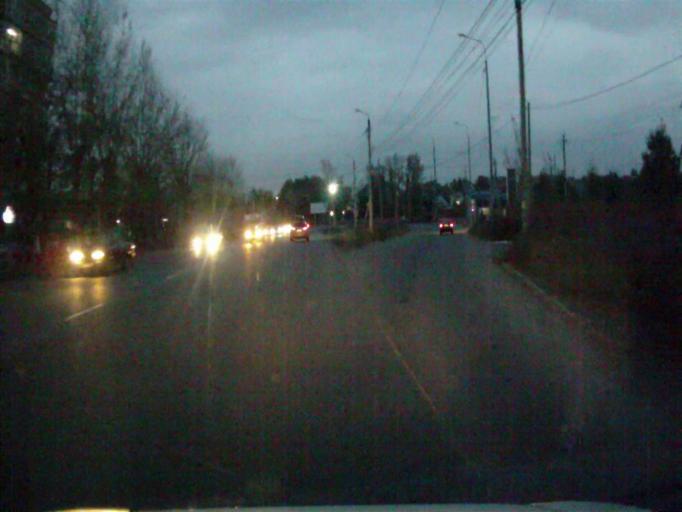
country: RU
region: Chelyabinsk
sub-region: Gorod Chelyabinsk
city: Chelyabinsk
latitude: 55.1584
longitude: 61.2978
